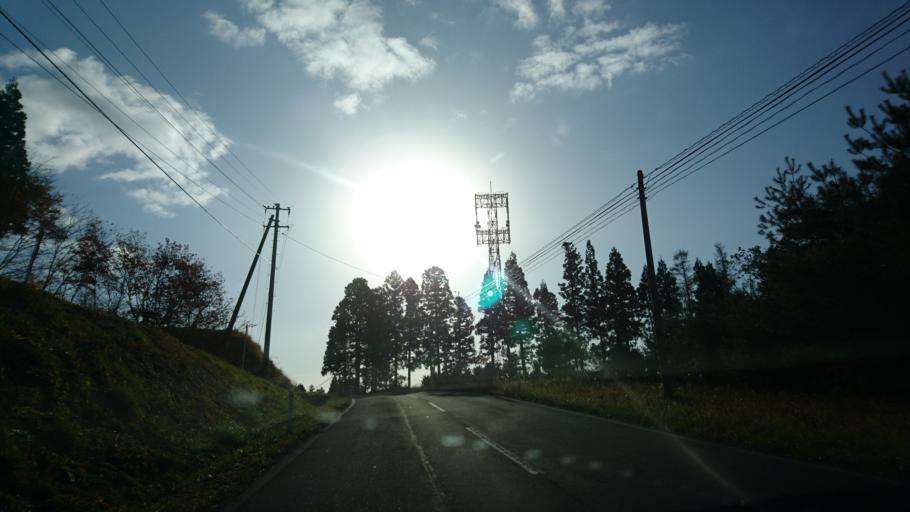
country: JP
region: Iwate
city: Ichinoseki
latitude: 38.8759
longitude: 141.2927
